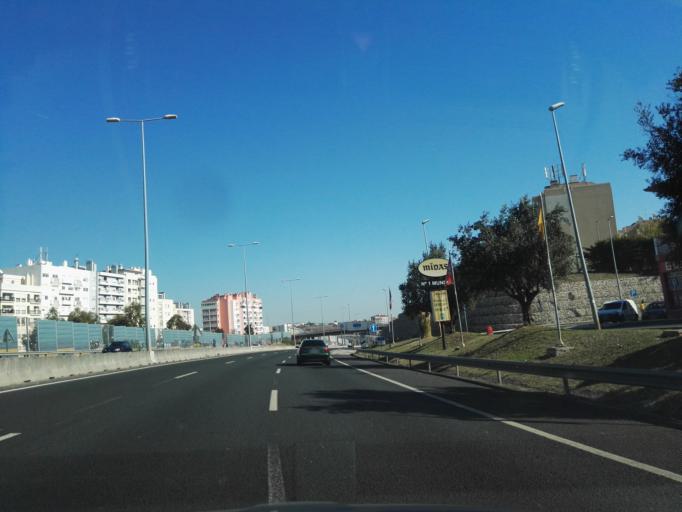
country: PT
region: Lisbon
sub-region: Odivelas
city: Olival do Basto
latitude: 38.7679
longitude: -9.1711
